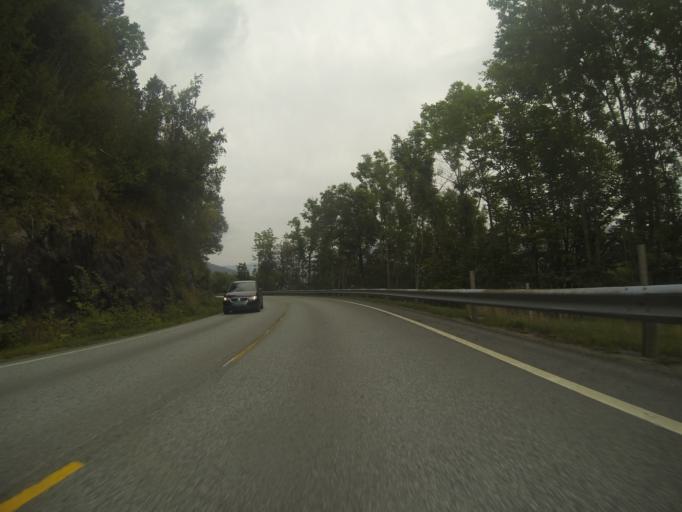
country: NO
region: Rogaland
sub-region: Suldal
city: Sand
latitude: 59.5637
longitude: 6.2729
